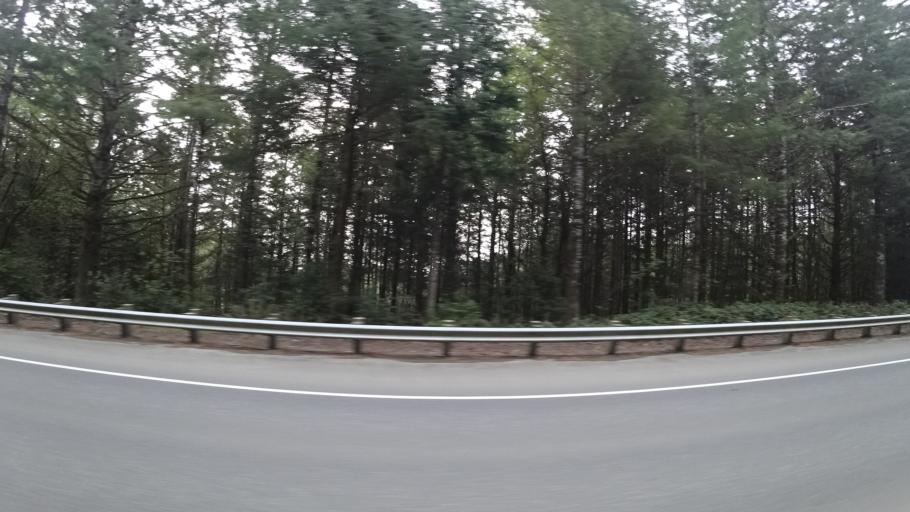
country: US
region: Oregon
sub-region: Coos County
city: Barview
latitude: 43.2488
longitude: -124.2868
